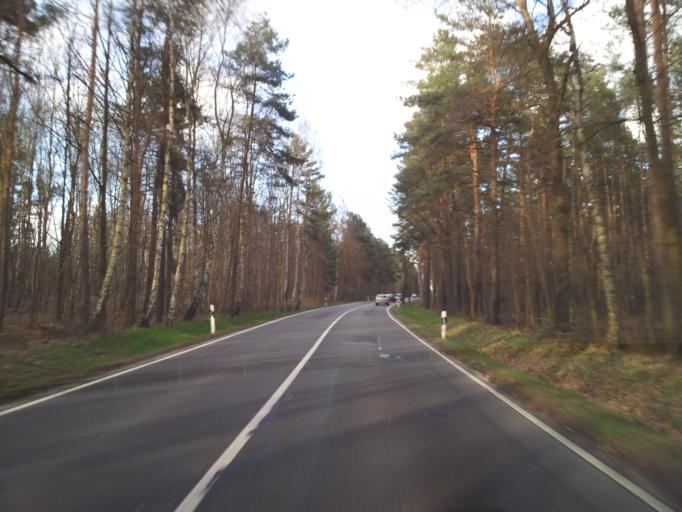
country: DE
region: Saxony
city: Schwepnitz
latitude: 51.3175
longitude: 13.9340
